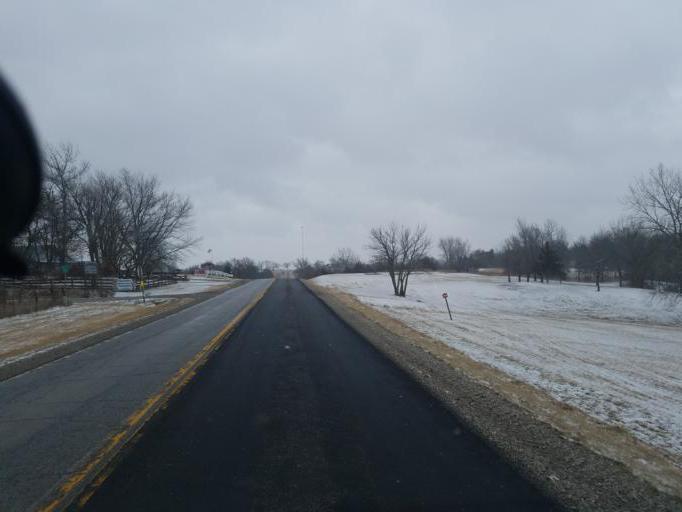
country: US
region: Missouri
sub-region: Putnam County
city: Unionville
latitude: 40.5227
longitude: -93.0126
